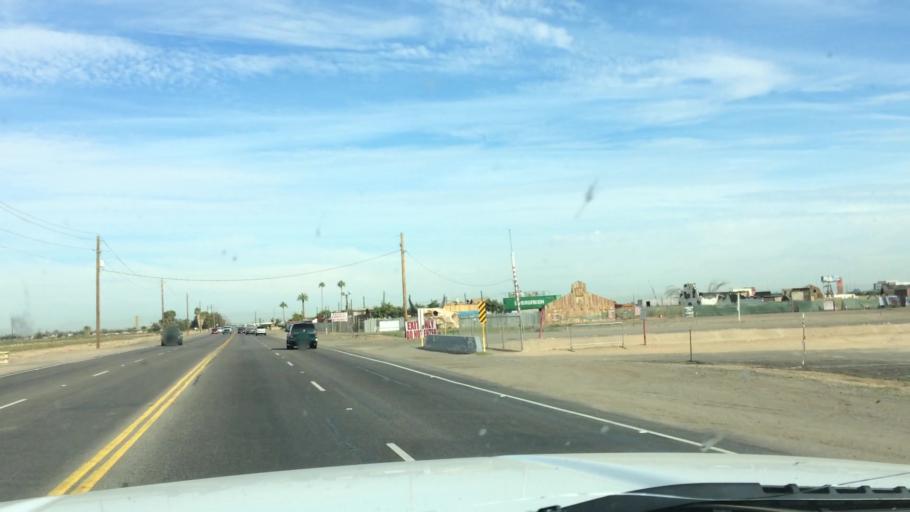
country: US
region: Arizona
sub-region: Maricopa County
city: Tolleson
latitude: 33.4682
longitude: -112.2725
